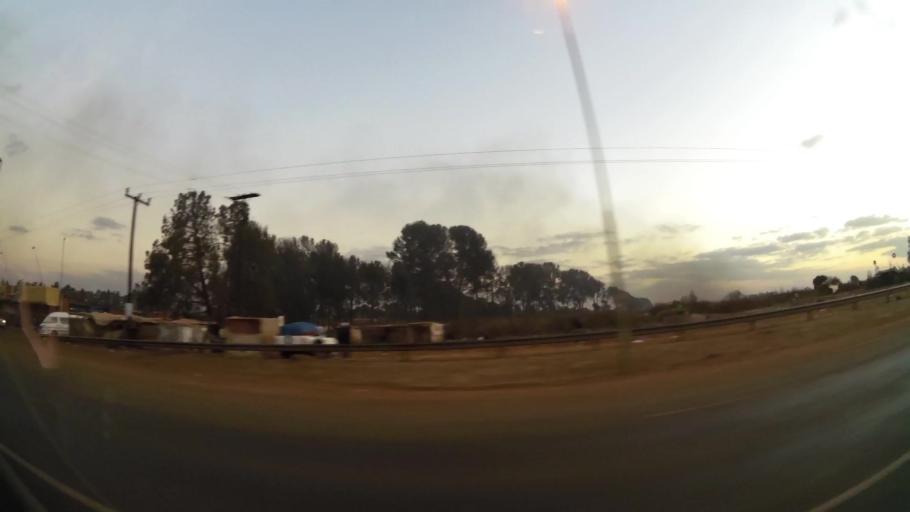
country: ZA
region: Gauteng
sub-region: West Rand District Municipality
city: Randfontein
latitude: -26.0799
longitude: 27.6538
